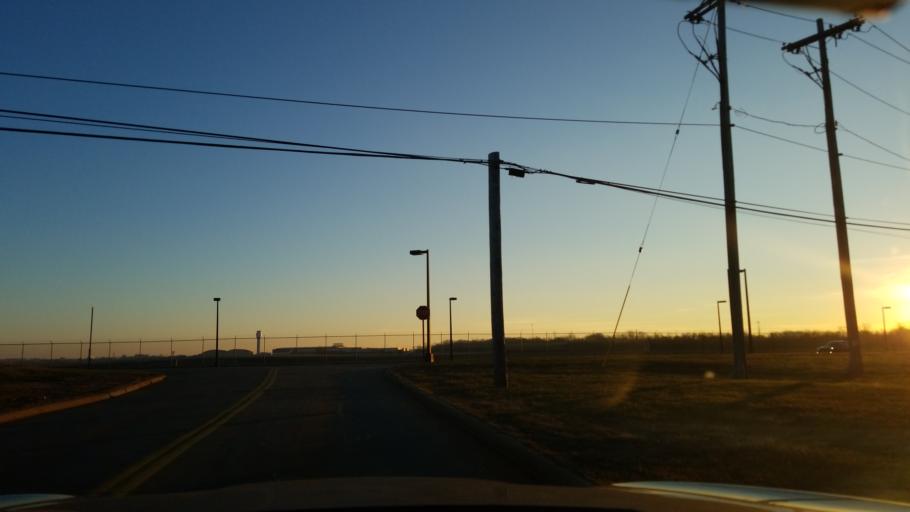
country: US
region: Ohio
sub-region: Cuyahoga County
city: Olmsted Falls
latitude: 41.3952
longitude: -81.8799
